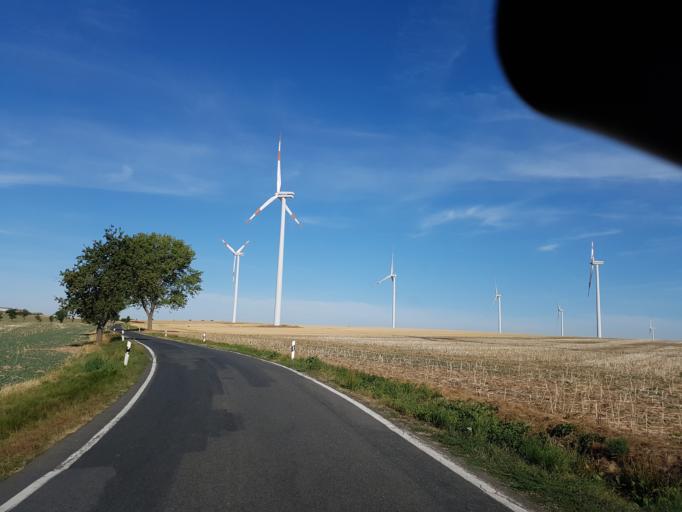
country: DE
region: Saxony
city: Naundorf
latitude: 51.2369
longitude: 13.1509
